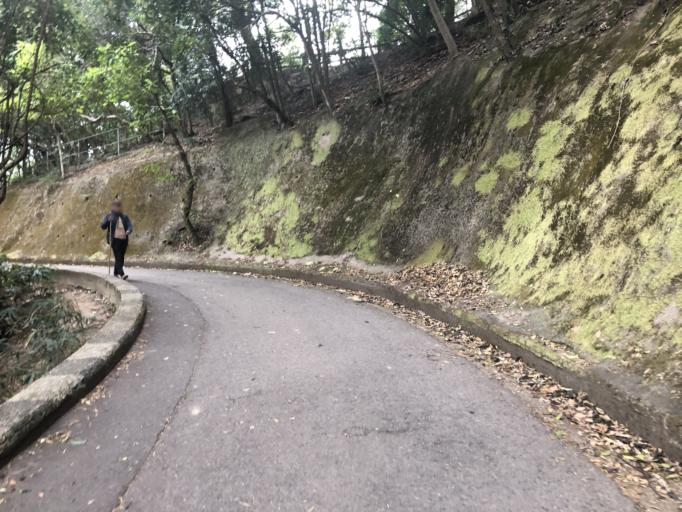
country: HK
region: Wanchai
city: Wan Chai
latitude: 22.2779
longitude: 114.2103
